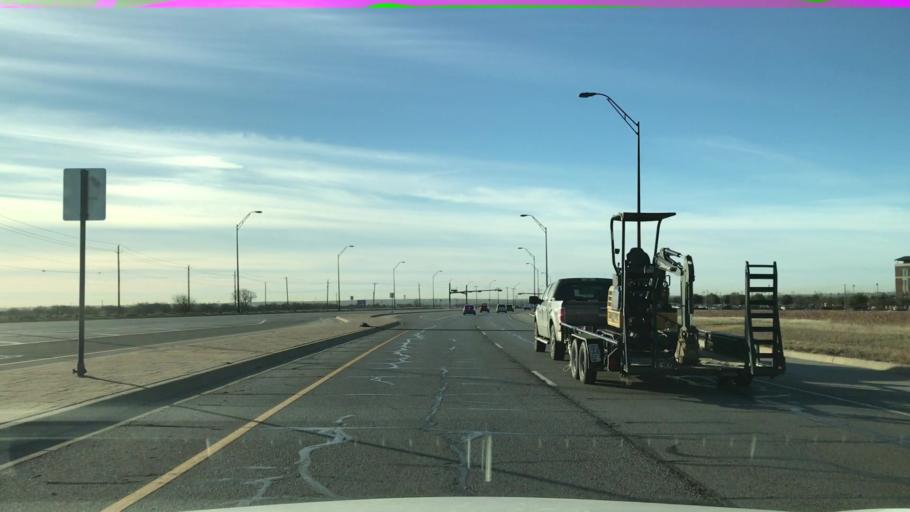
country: US
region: Texas
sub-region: Williamson County
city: Round Rock
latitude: 30.5616
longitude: -97.6463
